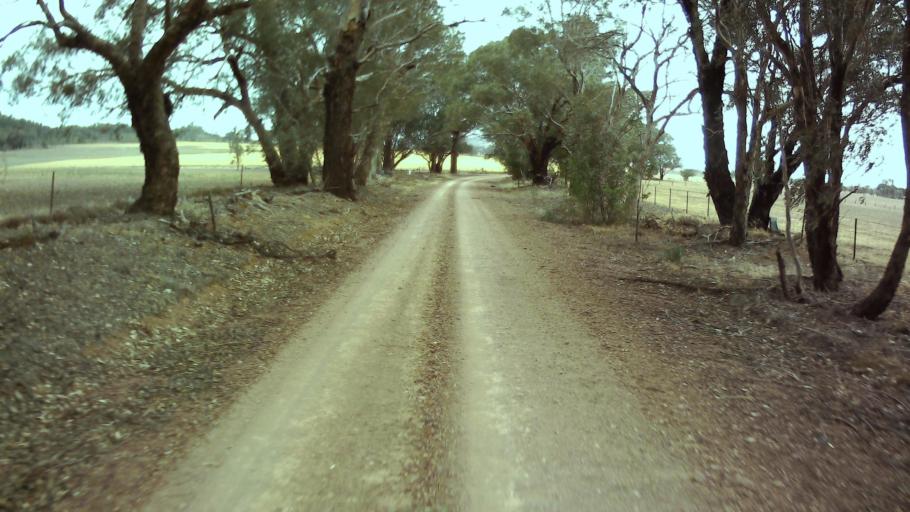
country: AU
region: New South Wales
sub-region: Weddin
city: Grenfell
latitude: -33.9154
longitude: 148.2882
